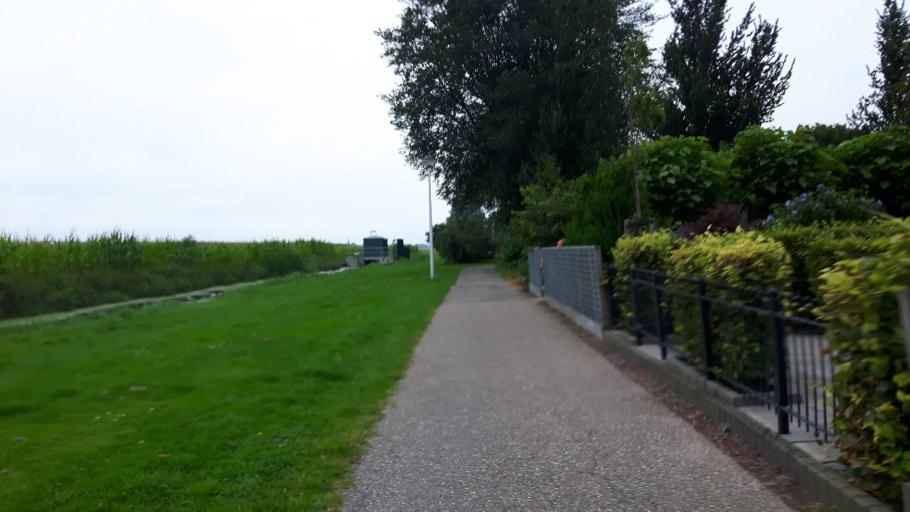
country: NL
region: South Holland
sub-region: Gemeente Nieuwkoop
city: Nieuwkoop
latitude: 52.1805
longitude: 4.7776
